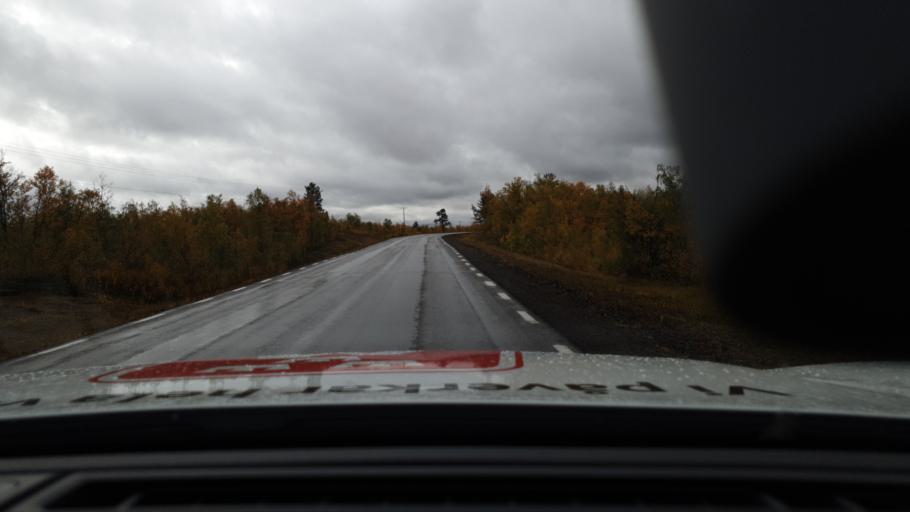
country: SE
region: Norrbotten
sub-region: Kiruna Kommun
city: Kiruna
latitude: 67.7824
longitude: 20.2262
